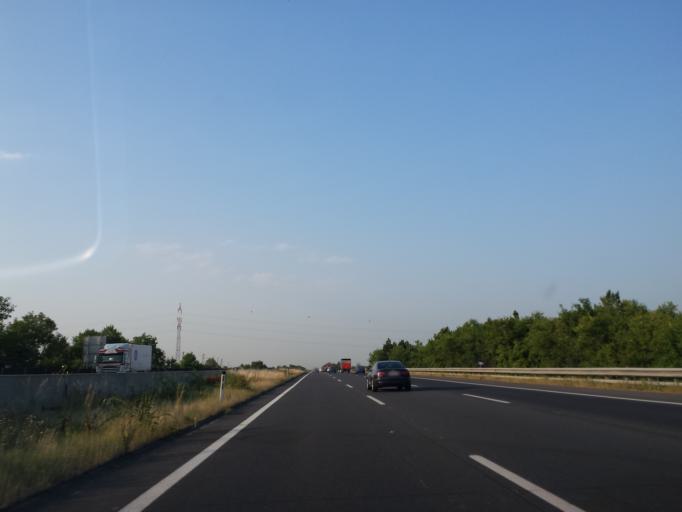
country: AT
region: Lower Austria
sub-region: Politischer Bezirk Baden
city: Leobersdorf
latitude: 47.9199
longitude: 16.2084
